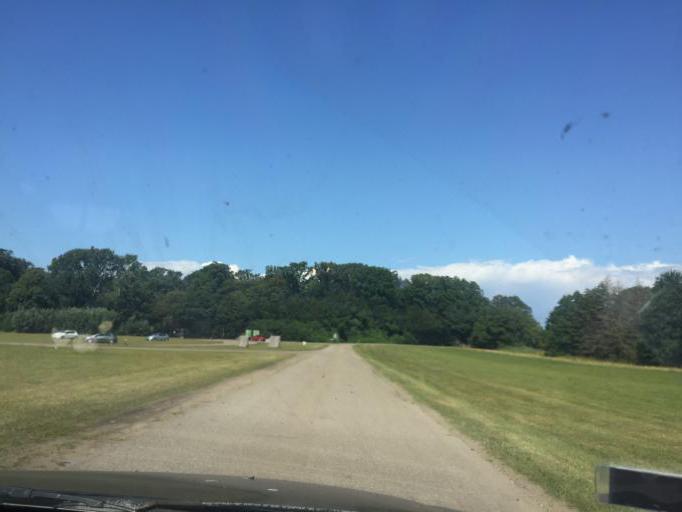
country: DK
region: Zealand
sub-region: Lolland Kommune
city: Maribo
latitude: 54.8213
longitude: 11.5152
